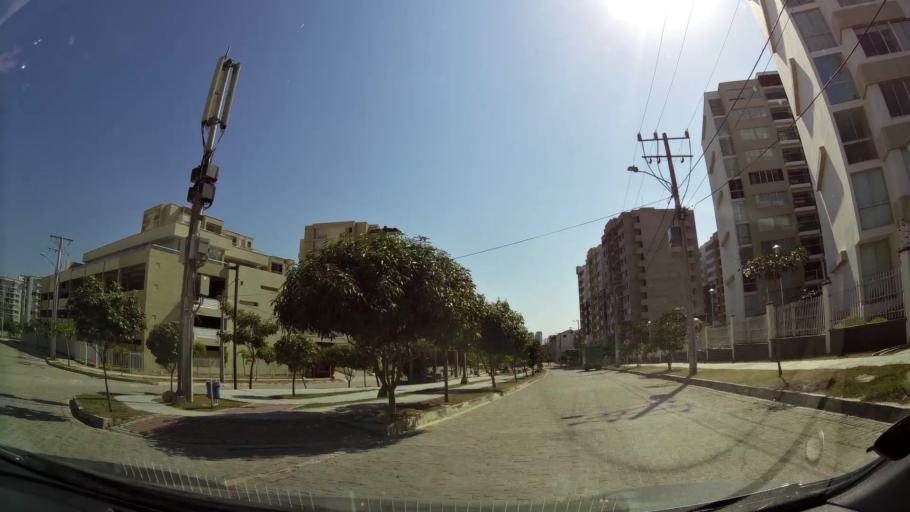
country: CO
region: Atlantico
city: Barranquilla
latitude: 11.0207
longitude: -74.8192
